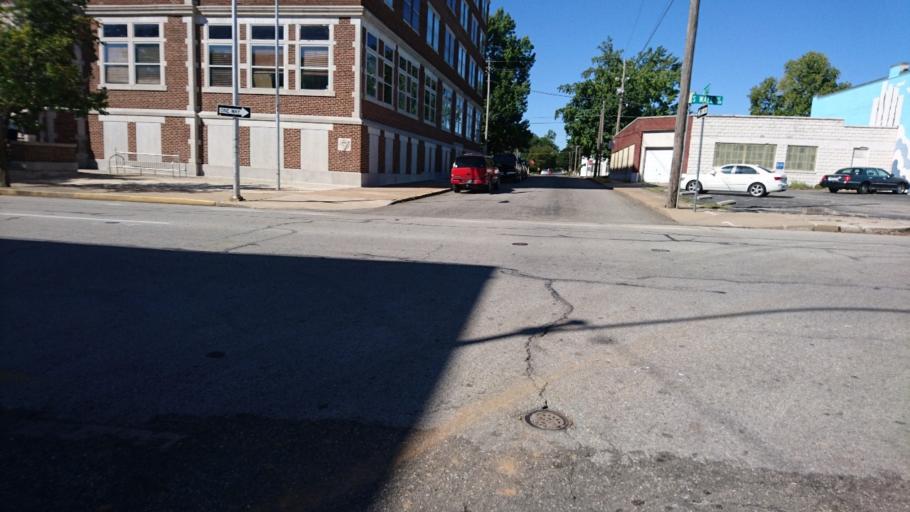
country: US
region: Missouri
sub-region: Jasper County
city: Joplin
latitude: 37.0868
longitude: -94.5155
